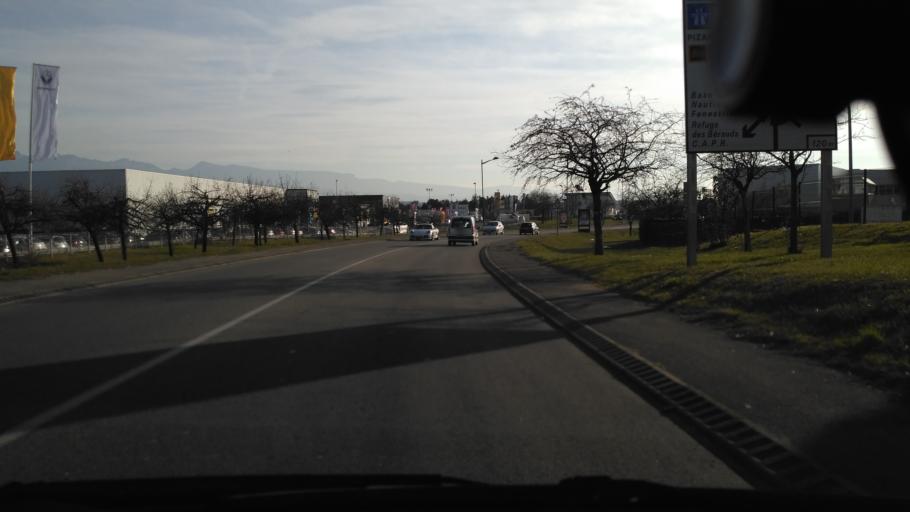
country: FR
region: Rhone-Alpes
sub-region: Departement de la Drome
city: Bourg-de-Peage
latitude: 45.0455
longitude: 5.0845
